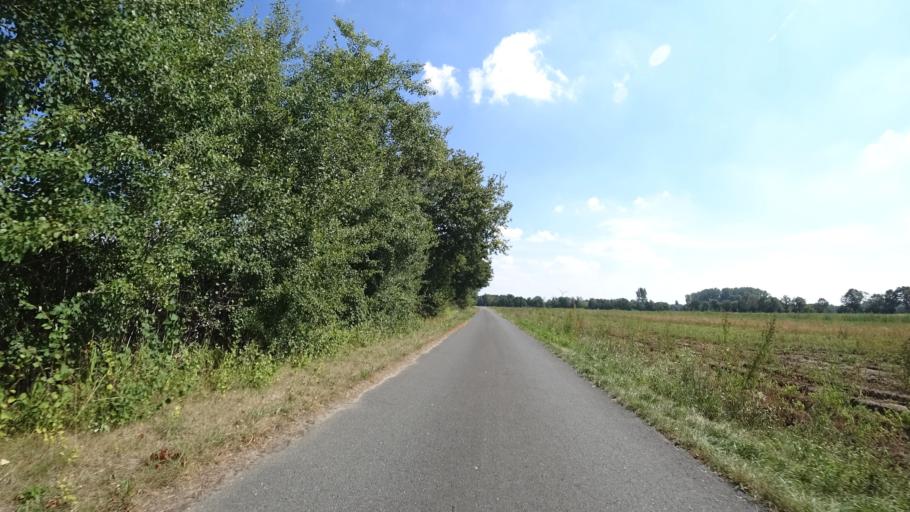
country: DE
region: North Rhine-Westphalia
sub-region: Regierungsbezirk Detmold
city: Rheda-Wiedenbruck
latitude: 51.8862
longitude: 8.2924
